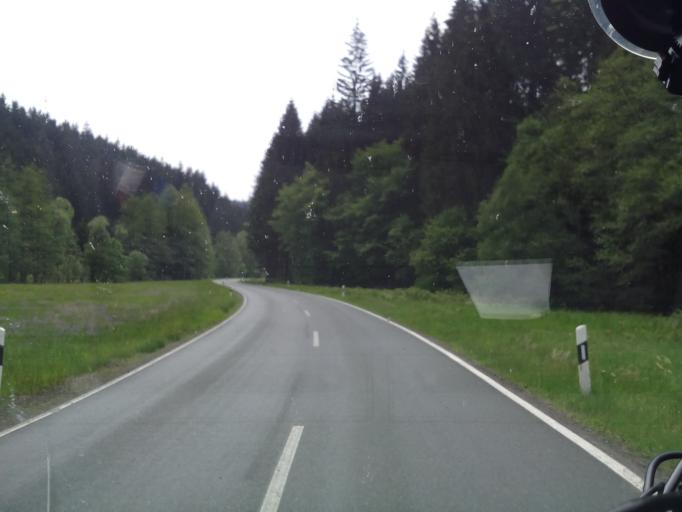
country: DE
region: Bavaria
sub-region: Upper Franconia
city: Steinwiesen
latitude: 50.2966
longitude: 11.4455
